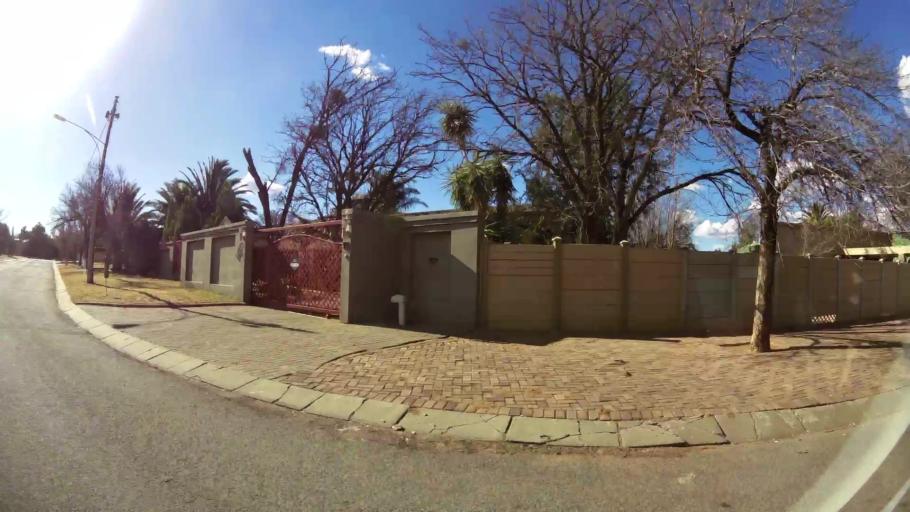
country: ZA
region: North-West
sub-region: Dr Kenneth Kaunda District Municipality
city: Klerksdorp
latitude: -26.8370
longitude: 26.6576
